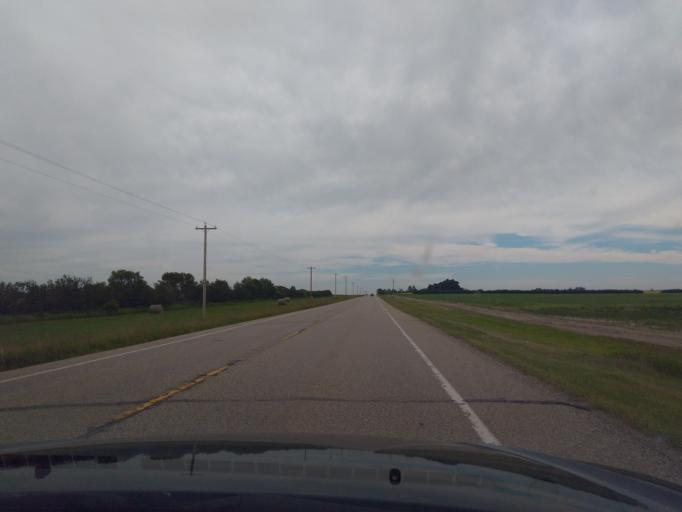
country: CA
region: Alberta
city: Irricana
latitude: 51.5034
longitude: -113.6343
